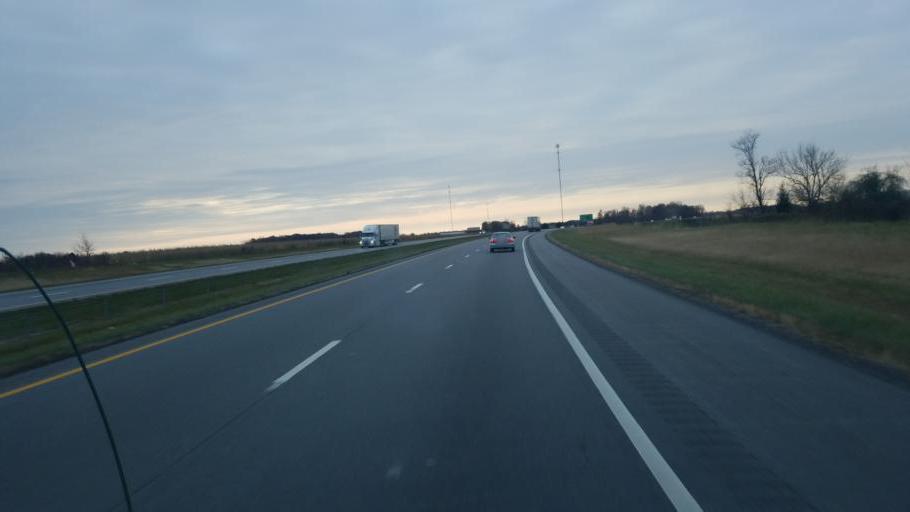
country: US
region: Ohio
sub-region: Auglaize County
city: Cridersville
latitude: 40.6438
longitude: -84.1314
